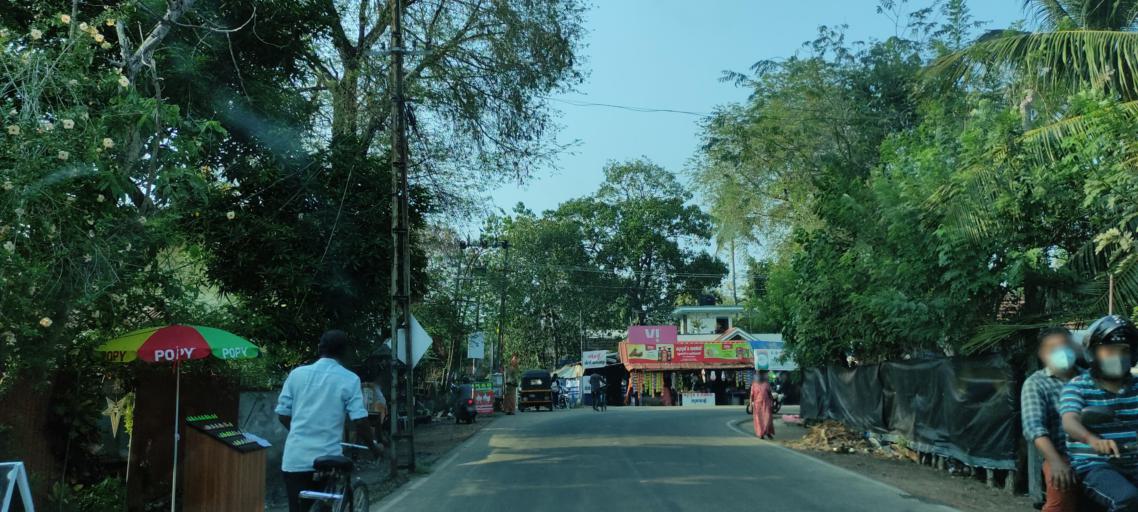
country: IN
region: Kerala
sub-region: Alappuzha
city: Alleppey
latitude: 9.5213
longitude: 76.3226
